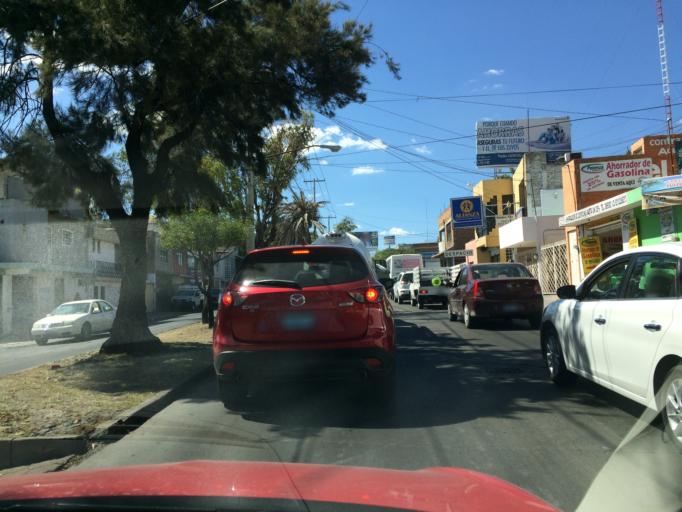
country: MX
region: Guanajuato
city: Leon
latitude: 21.1166
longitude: -101.6909
